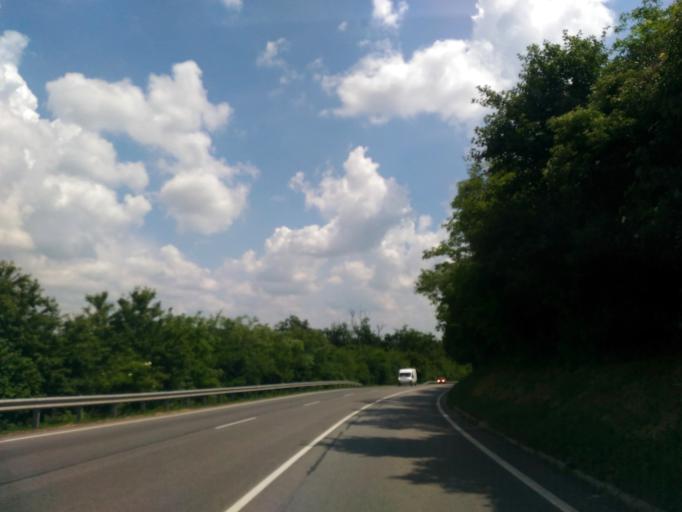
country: HU
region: Baranya
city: Pecs
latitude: 46.1269
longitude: 18.2568
